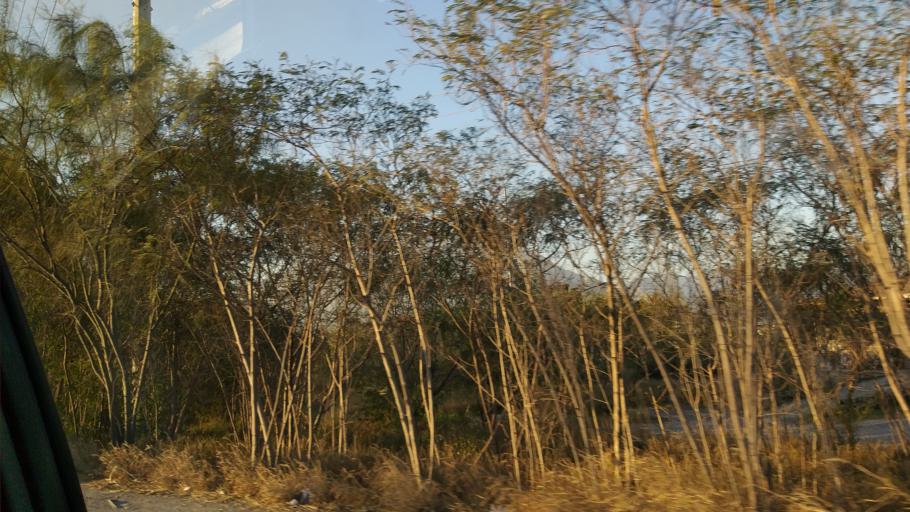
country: MX
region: Nuevo Leon
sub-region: Garcia
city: Parque Industrial Ciudad Mitras
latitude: 25.7789
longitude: -100.4485
